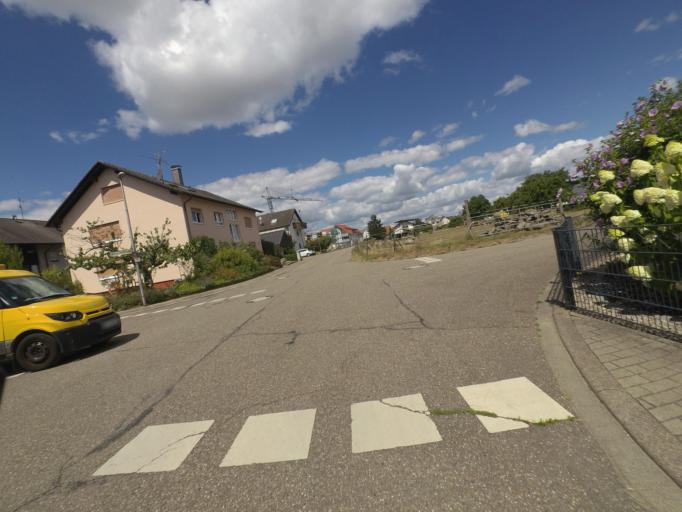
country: DE
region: Baden-Wuerttemberg
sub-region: Karlsruhe Region
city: Ottenhofen
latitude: 48.7517
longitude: 8.1006
